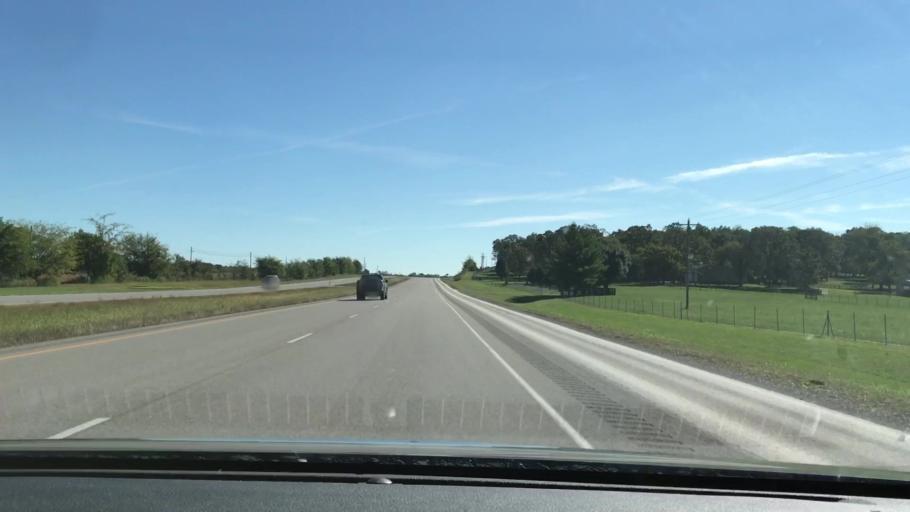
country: US
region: Kentucky
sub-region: Christian County
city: Hopkinsville
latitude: 36.8495
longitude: -87.3470
